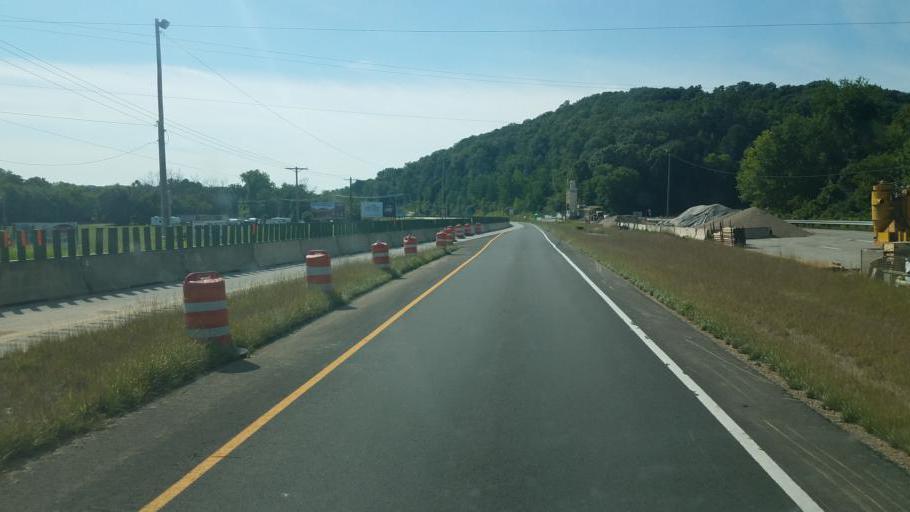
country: US
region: Ohio
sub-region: Athens County
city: Chauncey
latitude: 39.4038
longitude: -82.1698
